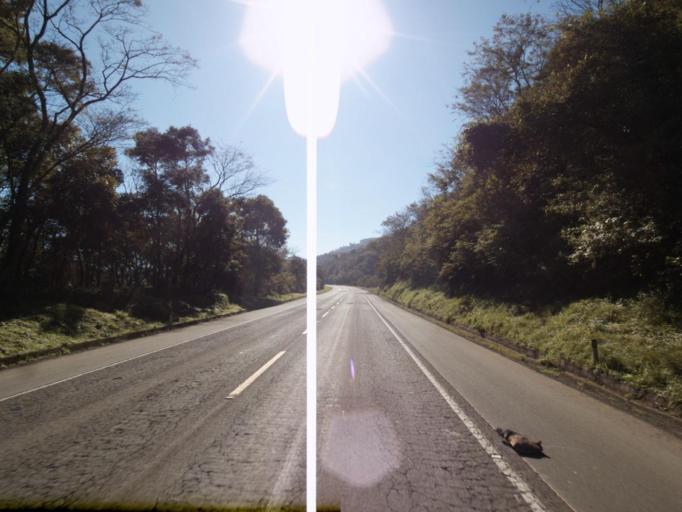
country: BR
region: Rio Grande do Sul
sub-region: Frederico Westphalen
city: Frederico Westphalen
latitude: -27.0139
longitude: -53.2263
